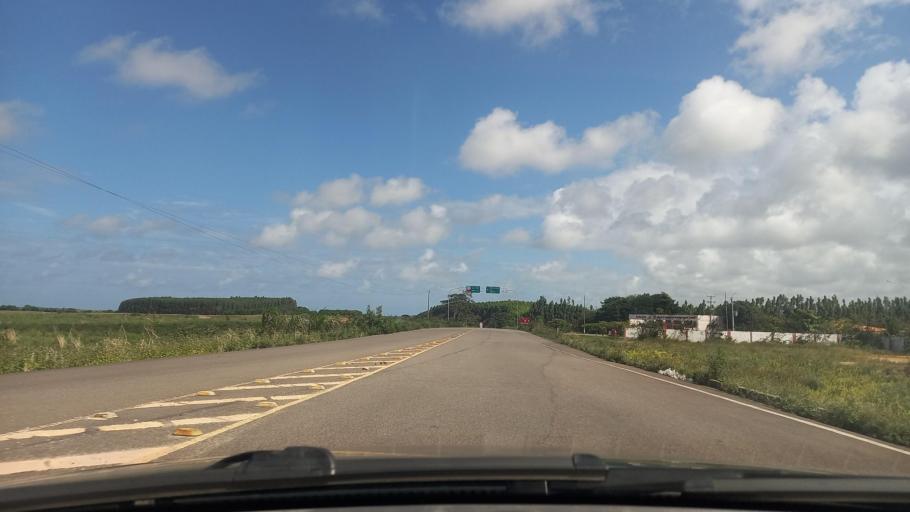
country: BR
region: Alagoas
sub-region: Marechal Deodoro
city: Marechal Deodoro
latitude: -9.8254
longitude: -35.9276
